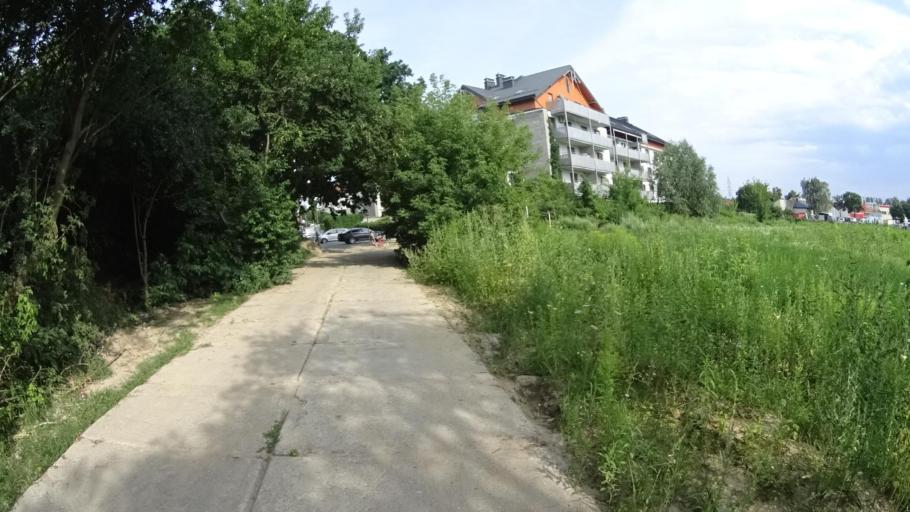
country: PL
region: Masovian Voivodeship
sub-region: Warszawa
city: Ursus
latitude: 52.2183
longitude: 20.8911
